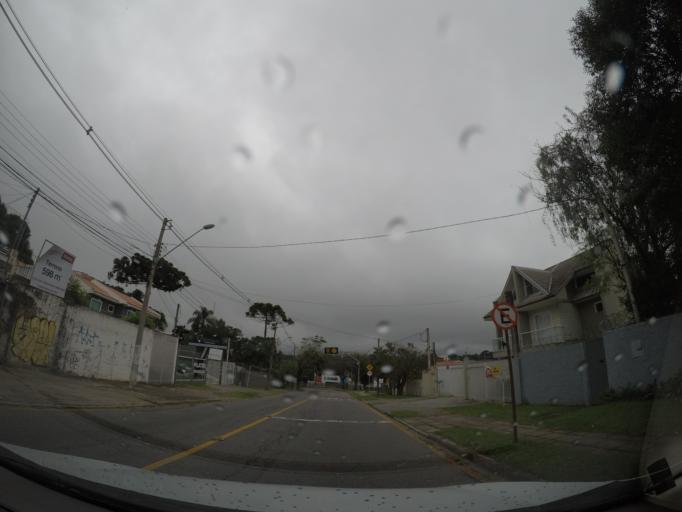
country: BR
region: Parana
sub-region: Curitiba
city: Curitiba
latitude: -25.4476
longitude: -49.3110
